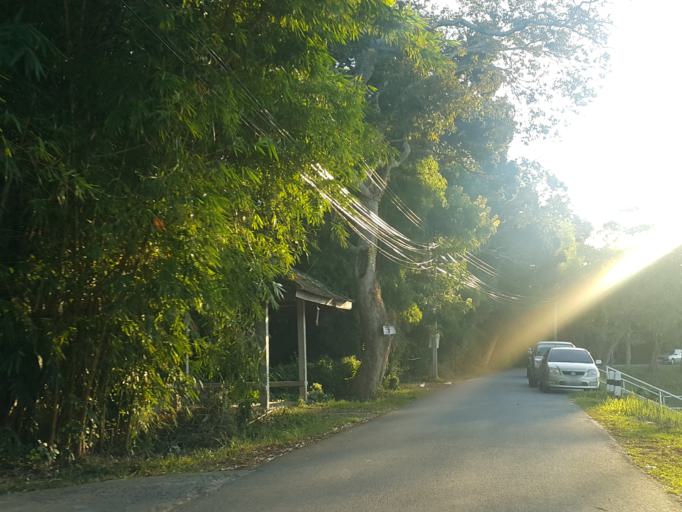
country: TH
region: Chiang Mai
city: San Sai
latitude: 18.8713
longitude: 99.1548
